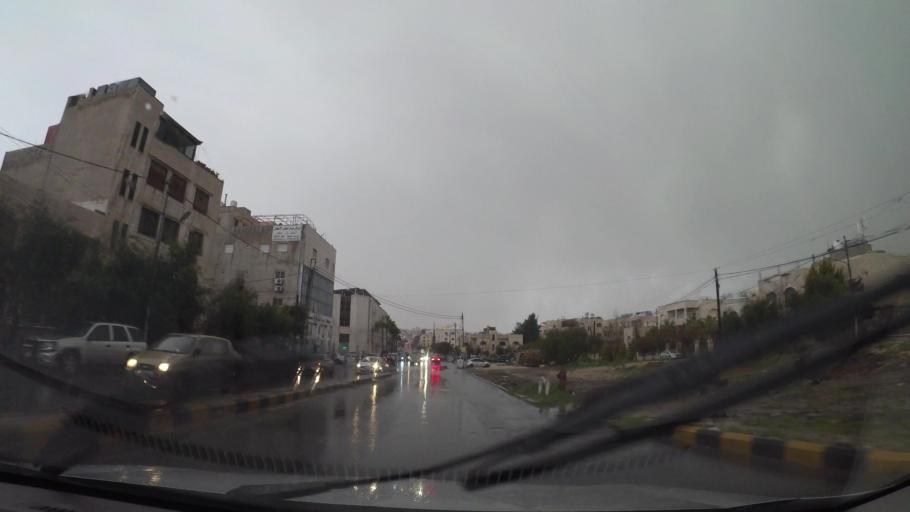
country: JO
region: Amman
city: Umm as Summaq
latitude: 31.8986
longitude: 35.8589
